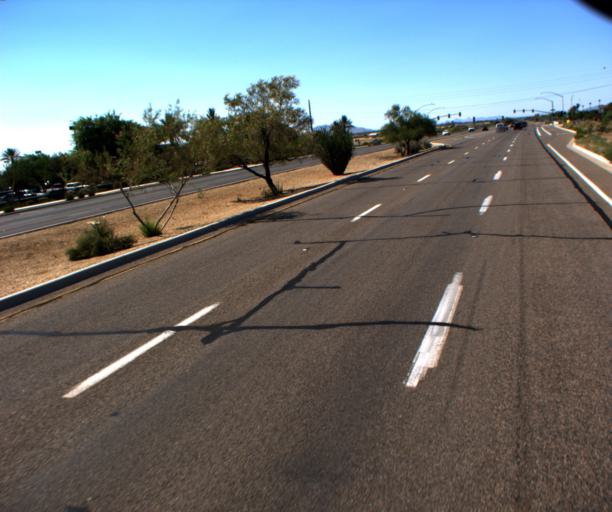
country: US
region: Arizona
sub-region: Pinal County
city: Casa Grande
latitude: 32.9406
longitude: -111.7569
